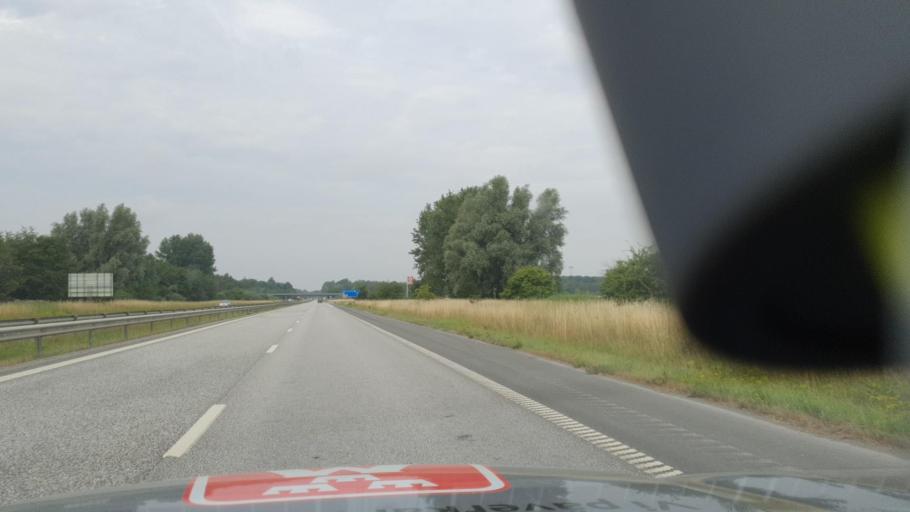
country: SE
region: Skane
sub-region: Kristianstads Kommun
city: Kristianstad
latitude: 56.0215
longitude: 14.1833
